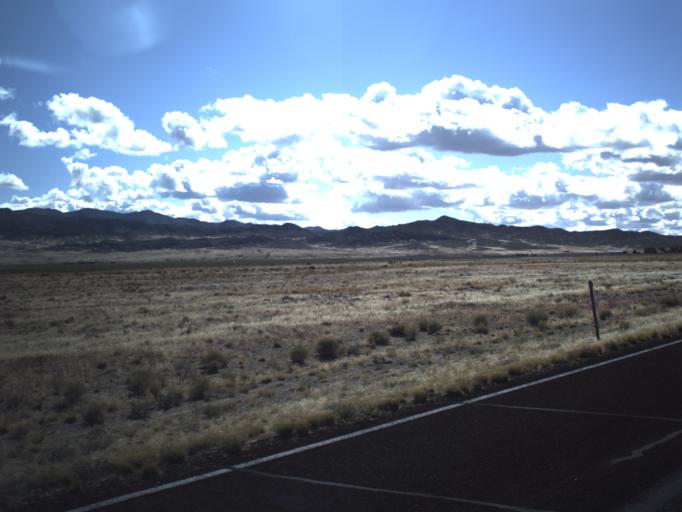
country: US
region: Nevada
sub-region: White Pine County
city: McGill
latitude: 38.9672
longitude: -114.0338
